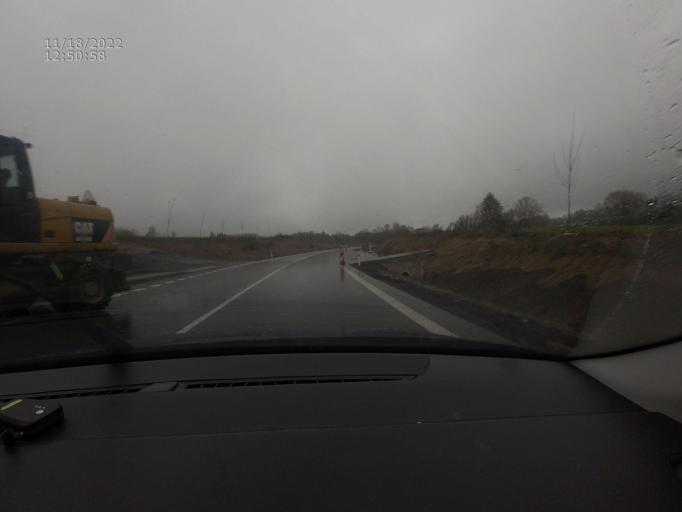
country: CZ
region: Plzensky
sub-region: Okres Klatovy
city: Kolinec
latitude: 49.3282
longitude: 13.4380
